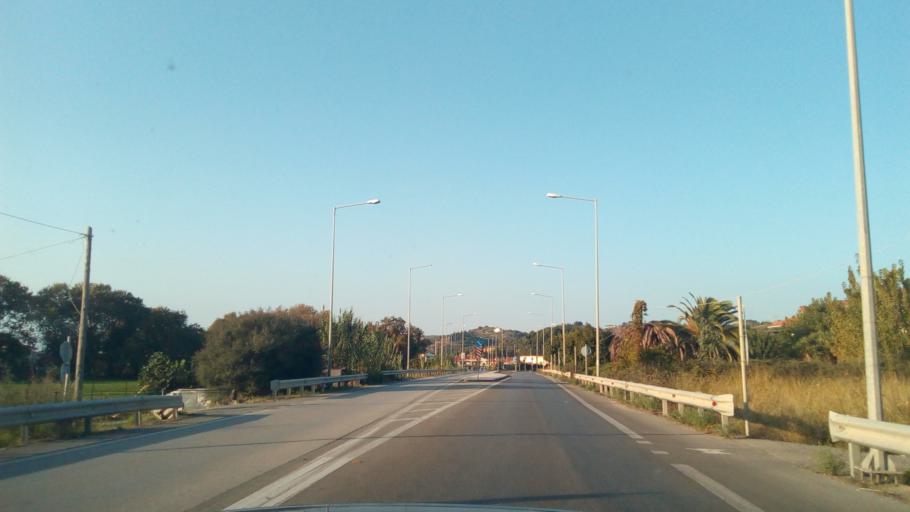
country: GR
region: West Greece
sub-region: Nomos Aitolias kai Akarnanias
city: Antirrio
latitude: 38.3716
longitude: 21.7830
